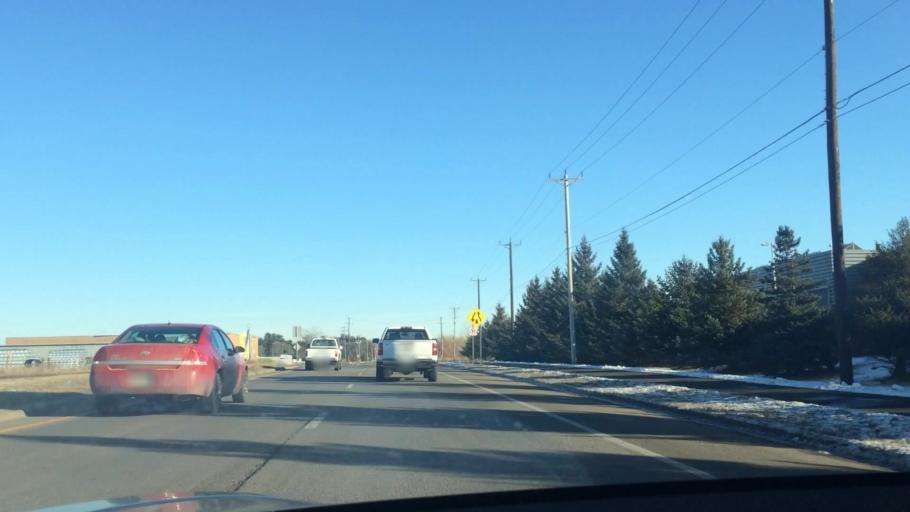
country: US
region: Minnesota
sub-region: Anoka County
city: Lexington
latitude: 45.1242
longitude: -93.1821
